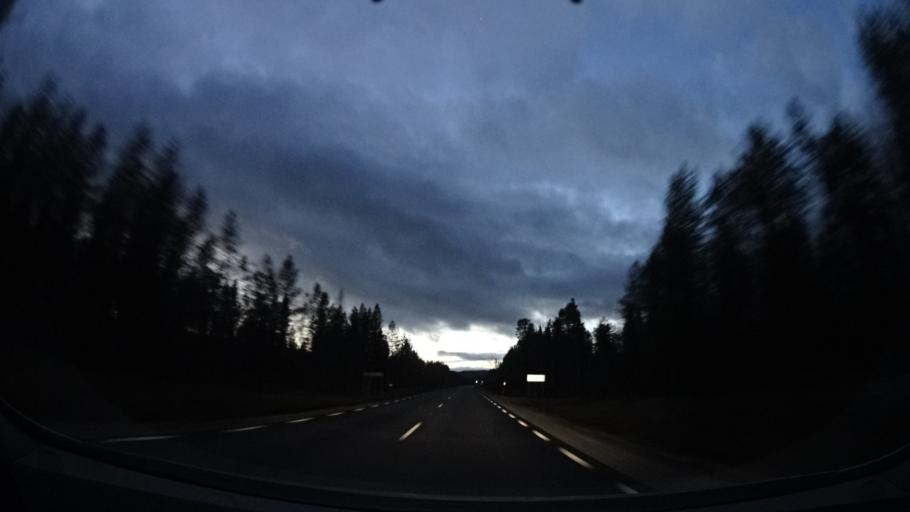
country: SE
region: Vaesterbotten
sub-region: Dorotea Kommun
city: Dorotea
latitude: 64.2409
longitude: 16.7182
